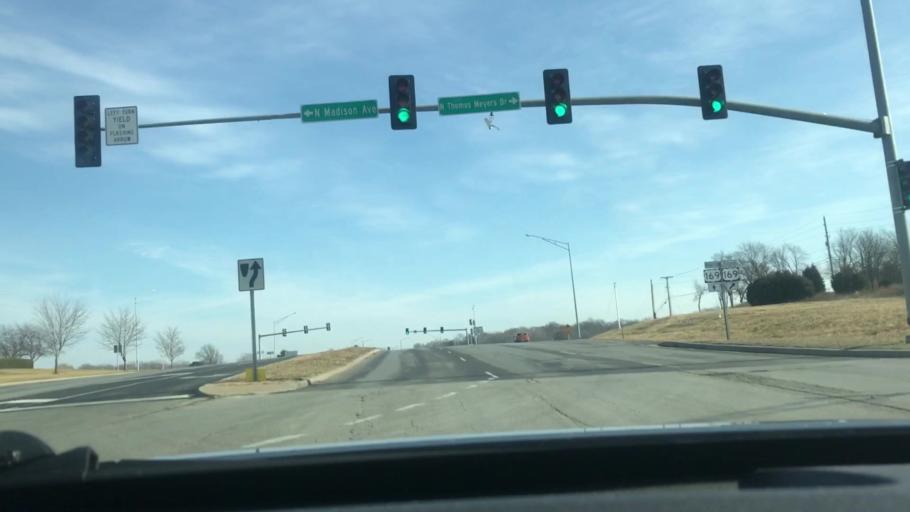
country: US
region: Missouri
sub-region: Clay County
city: Gladstone
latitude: 39.2464
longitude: -94.5946
